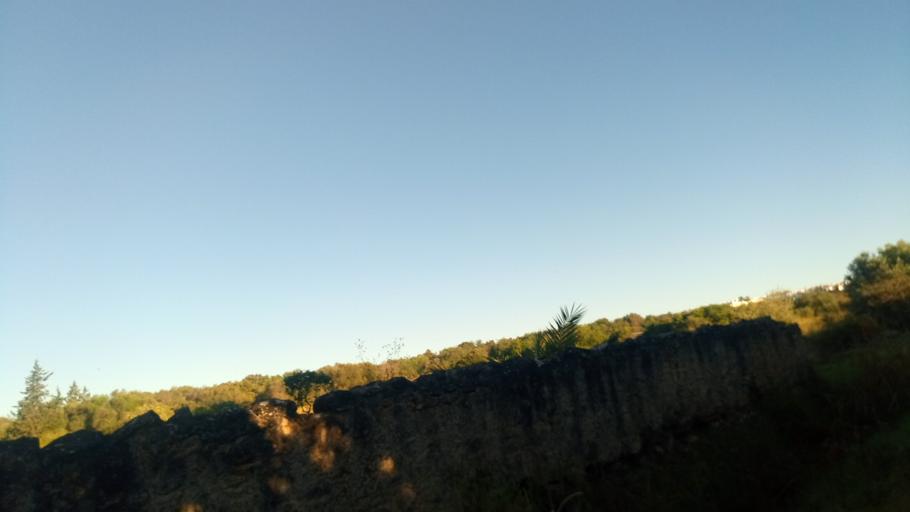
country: PT
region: Faro
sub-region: Tavira
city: Tavira
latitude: 37.1367
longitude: -7.6046
